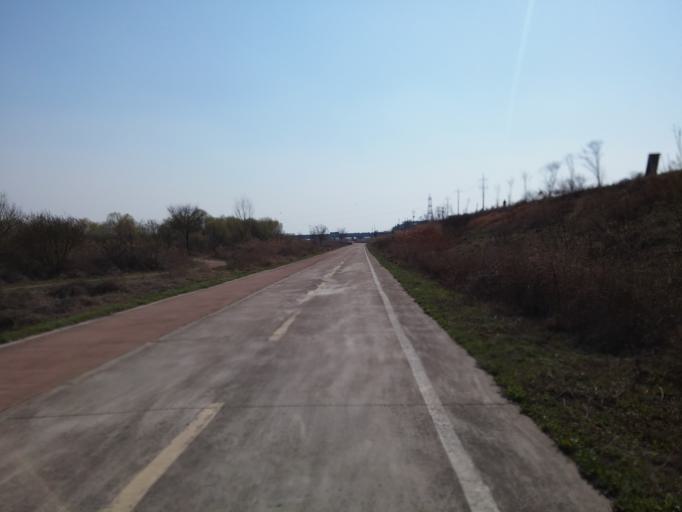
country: KR
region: Chungcheongbuk-do
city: Cheongju-si
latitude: 36.6564
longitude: 127.3789
